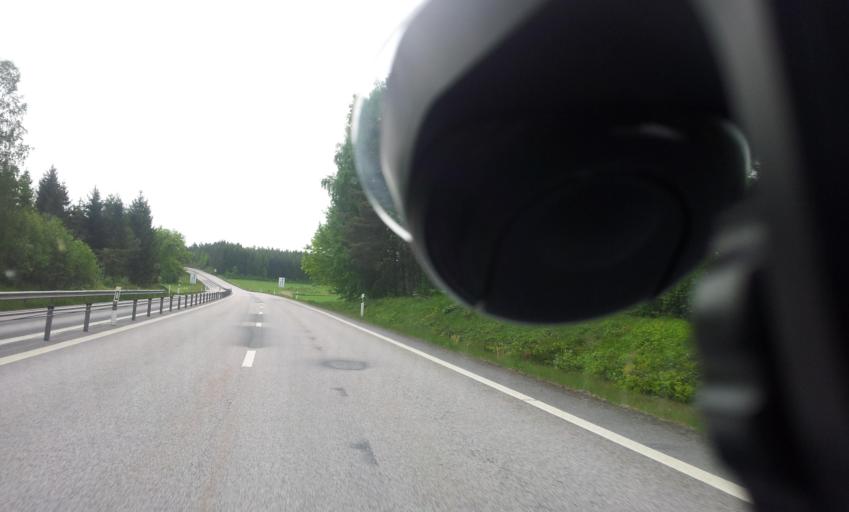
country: SE
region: Kalmar
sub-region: Vasterviks Kommun
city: Forserum
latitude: 58.0714
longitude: 16.5194
